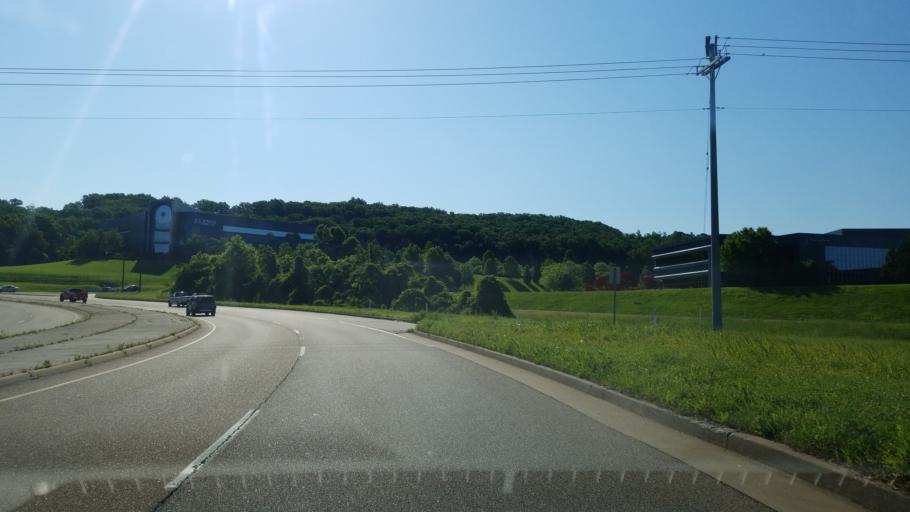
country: US
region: Tennessee
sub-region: Hamilton County
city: Harrison
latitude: 35.0587
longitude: -85.1298
